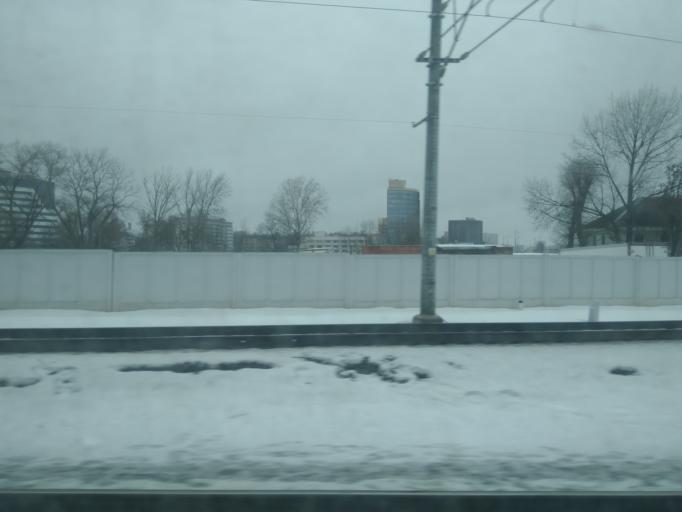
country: BY
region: Minsk
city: Minsk
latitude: 53.8916
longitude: 27.5339
